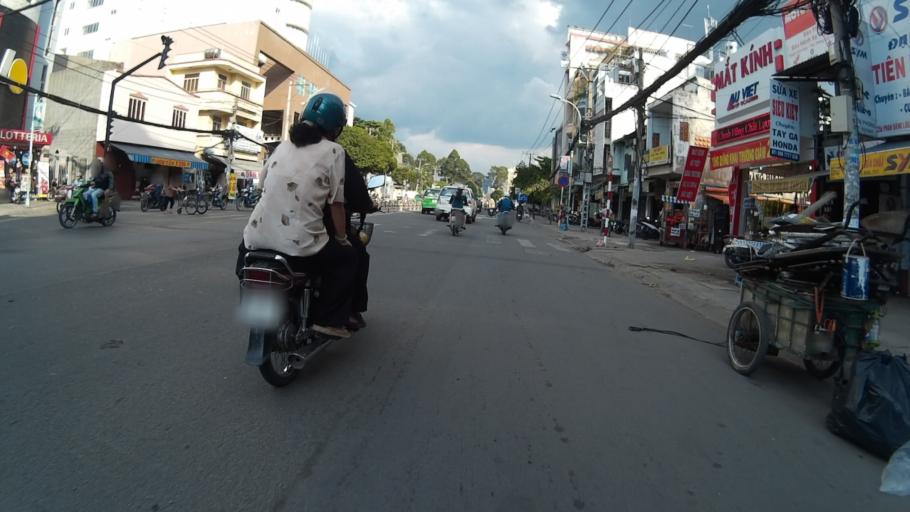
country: VN
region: Ho Chi Minh City
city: Quan Binh Thanh
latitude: 10.8031
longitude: 106.6924
